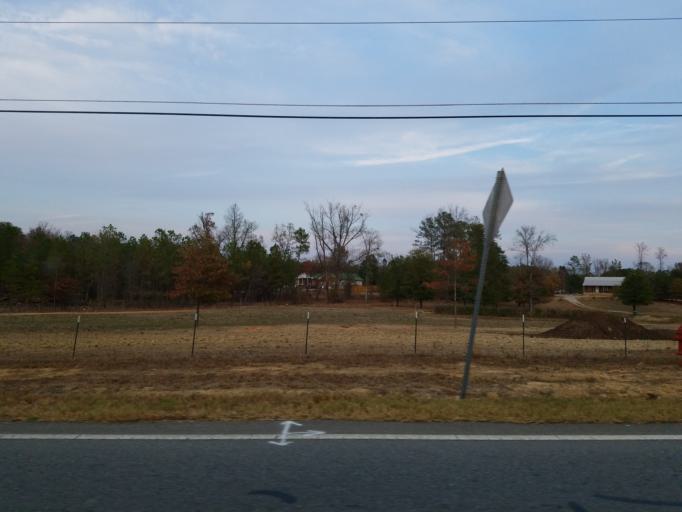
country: US
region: Georgia
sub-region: Gordon County
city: Calhoun
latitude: 34.5996
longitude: -84.9127
